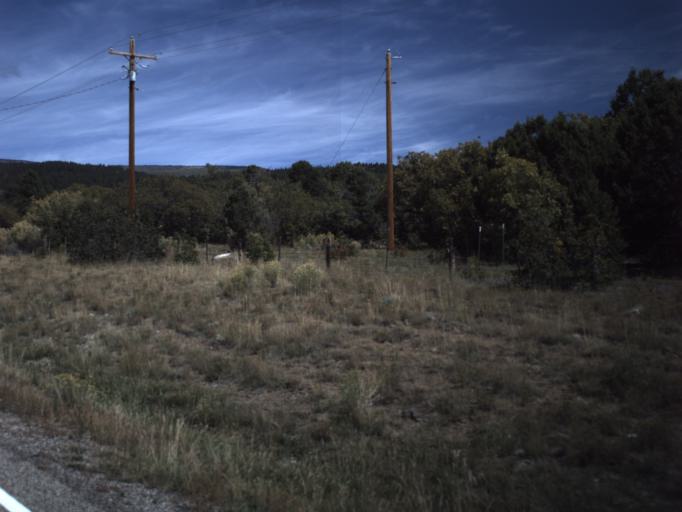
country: US
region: Utah
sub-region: Wayne County
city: Loa
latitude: 37.9764
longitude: -111.4310
